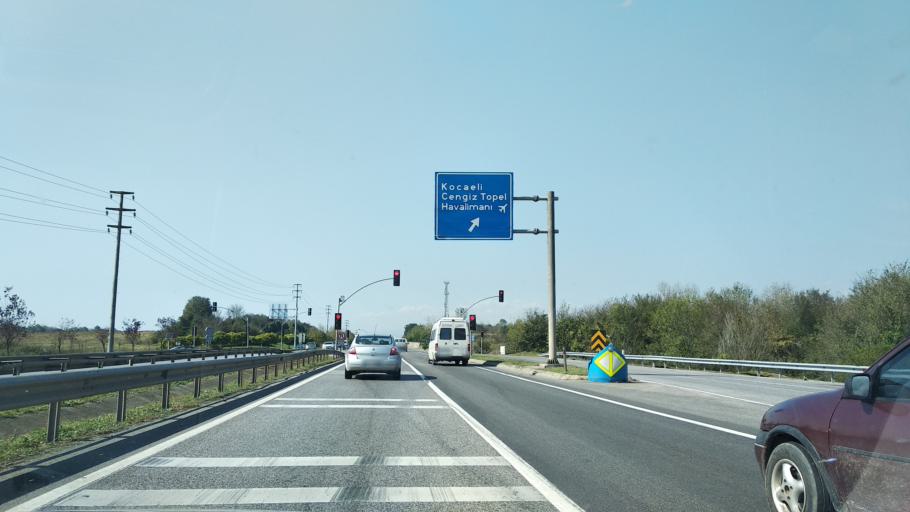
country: TR
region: Kocaeli
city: Derbent
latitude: 40.7434
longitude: 30.0819
